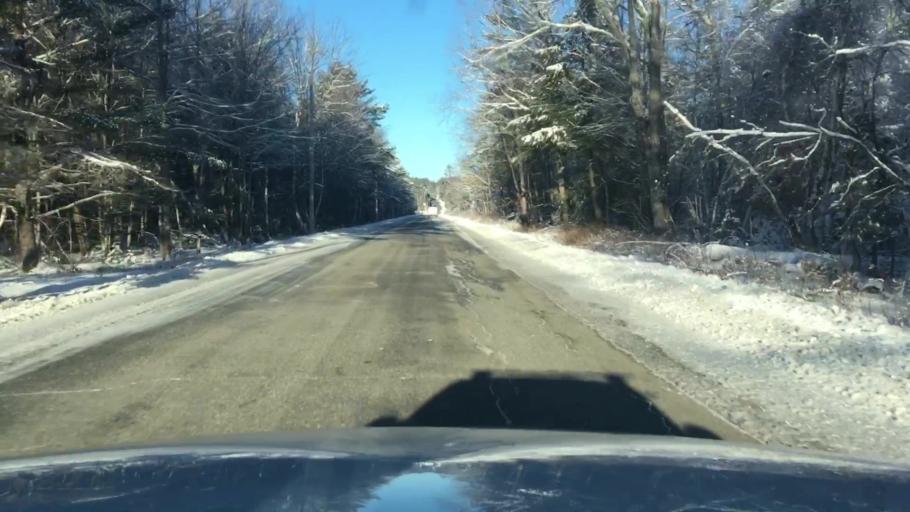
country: US
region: Maine
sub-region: Kennebec County
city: Belgrade
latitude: 44.4114
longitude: -69.8679
